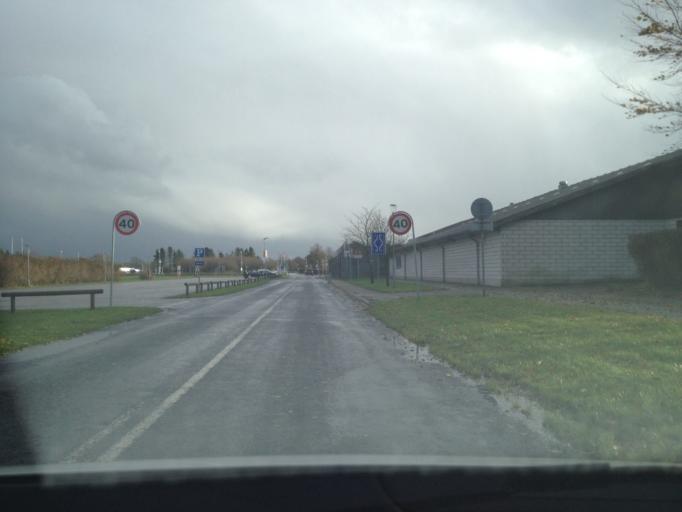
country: DK
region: South Denmark
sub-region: Tonder Kommune
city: Sherrebek
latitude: 55.0515
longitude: 8.8250
